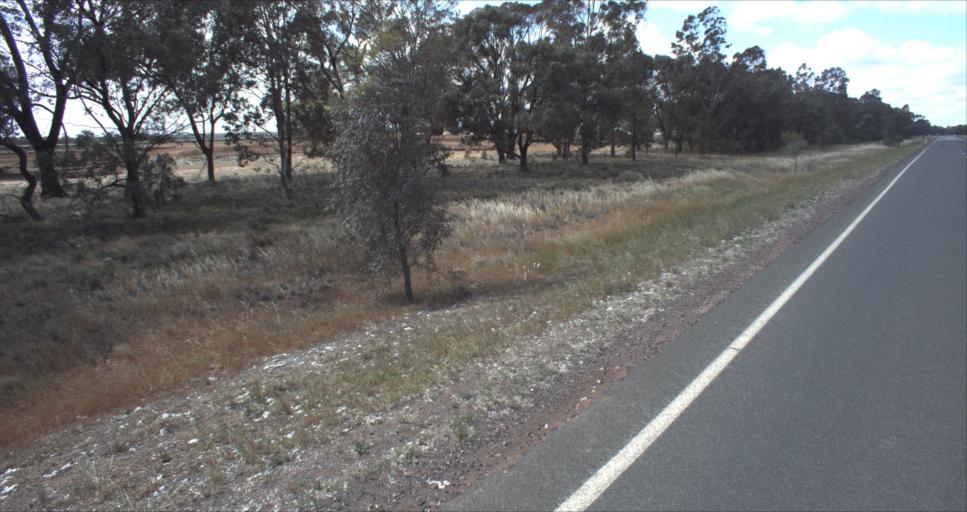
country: AU
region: New South Wales
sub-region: Murrumbidgee Shire
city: Darlington Point
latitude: -34.5881
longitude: 146.1640
